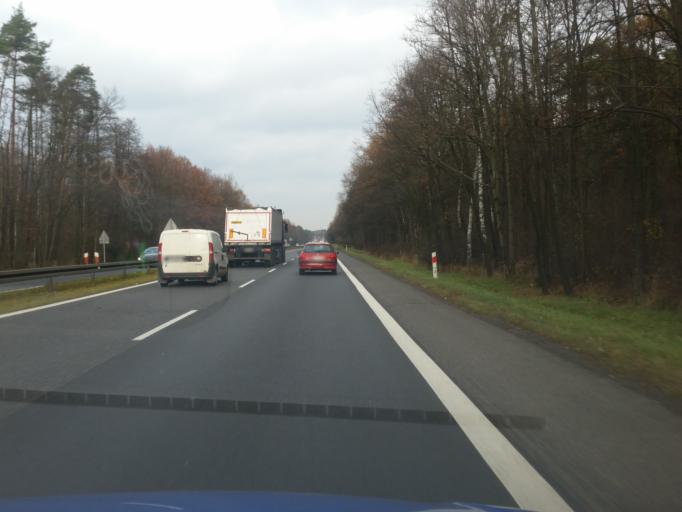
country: PL
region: Silesian Voivodeship
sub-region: Powiat czestochowski
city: Kamienica Polska
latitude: 50.6433
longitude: 19.1355
